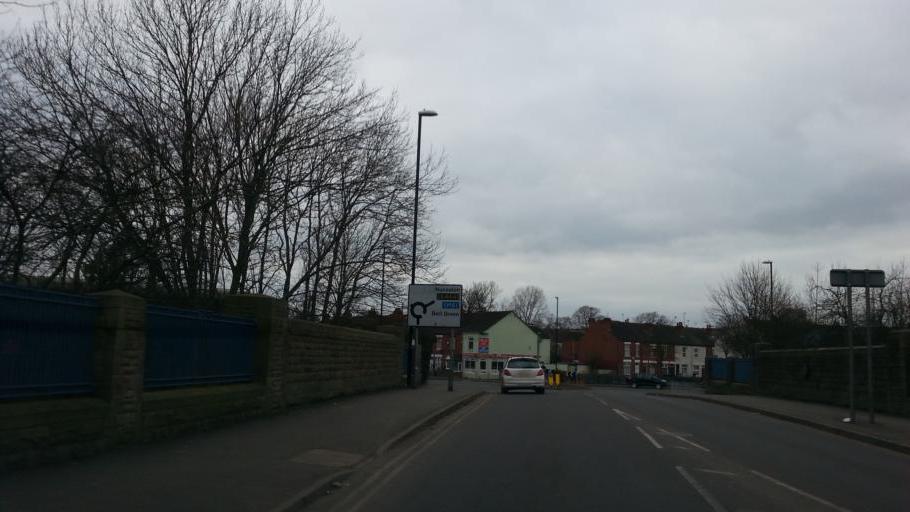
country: GB
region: England
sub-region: Coventry
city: Coventry
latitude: 52.4204
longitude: -1.4881
